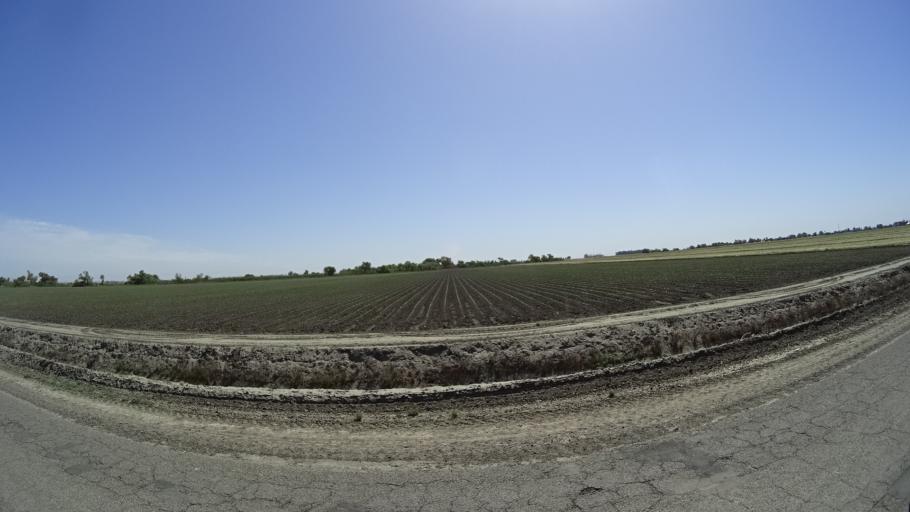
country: US
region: California
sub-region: Kings County
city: Stratford
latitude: 36.2060
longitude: -119.8341
